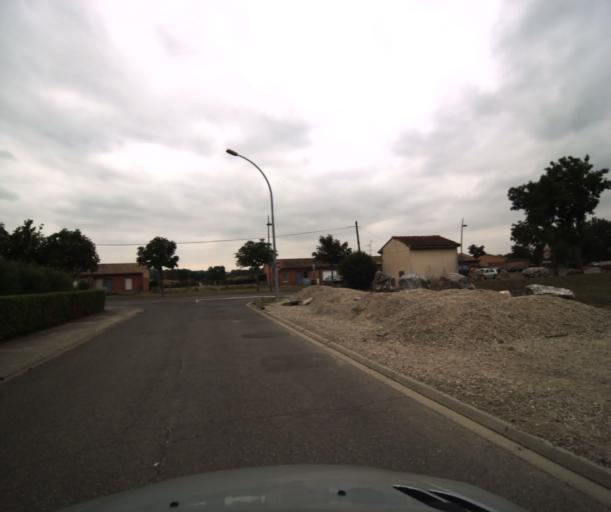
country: FR
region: Midi-Pyrenees
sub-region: Departement de la Haute-Garonne
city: Portet-sur-Garonne
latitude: 43.5420
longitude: 1.4082
